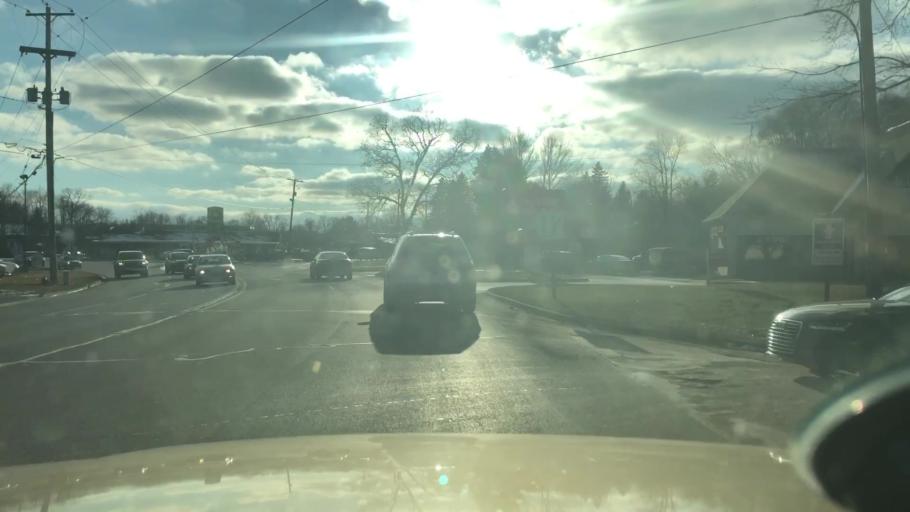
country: US
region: Michigan
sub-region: Jackson County
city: Vandercook Lake
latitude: 42.2012
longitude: -84.4378
